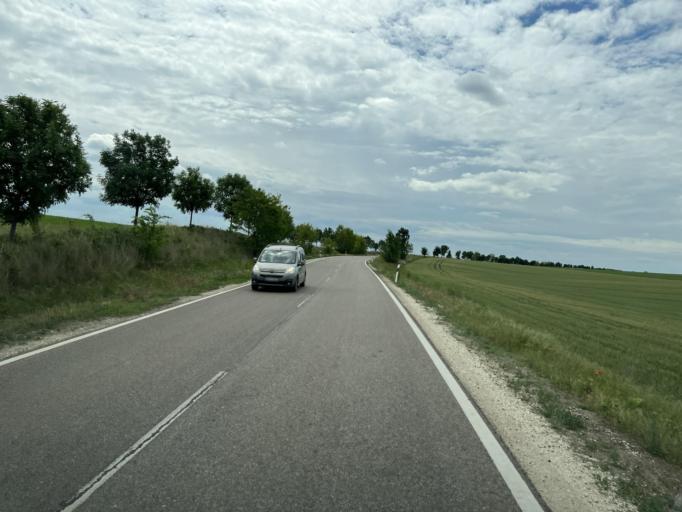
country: HU
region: Pest
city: Zsambok
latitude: 47.5214
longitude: 19.5993
